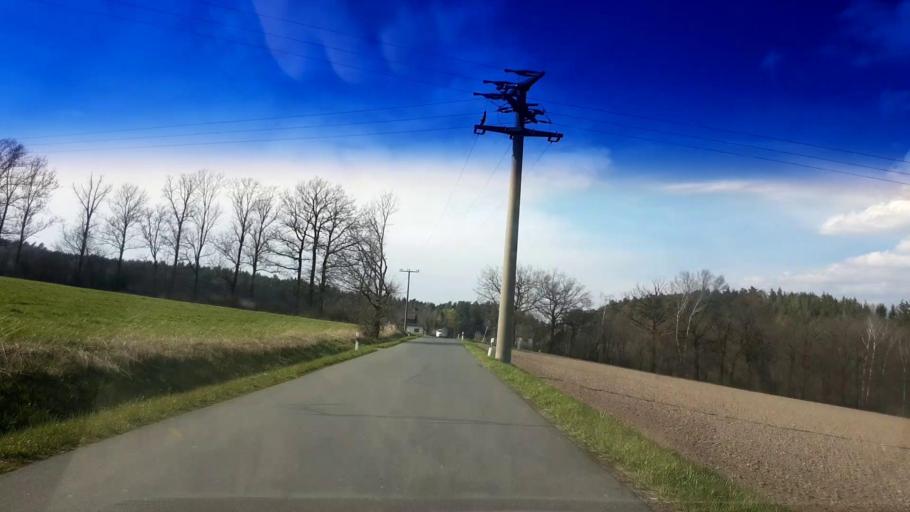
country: DE
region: Bavaria
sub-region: Upper Franconia
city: Himmelkron
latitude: 50.0314
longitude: 11.6177
